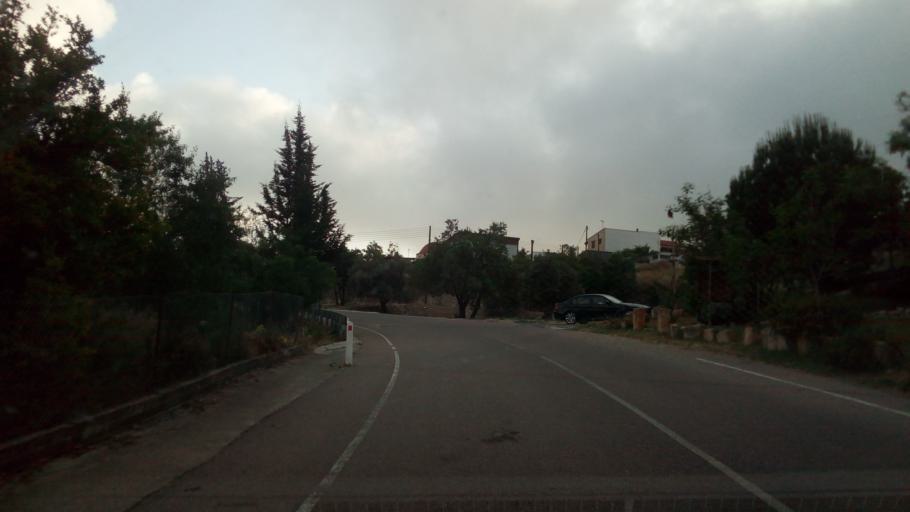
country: CY
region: Limassol
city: Pachna
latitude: 34.8416
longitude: 32.6923
